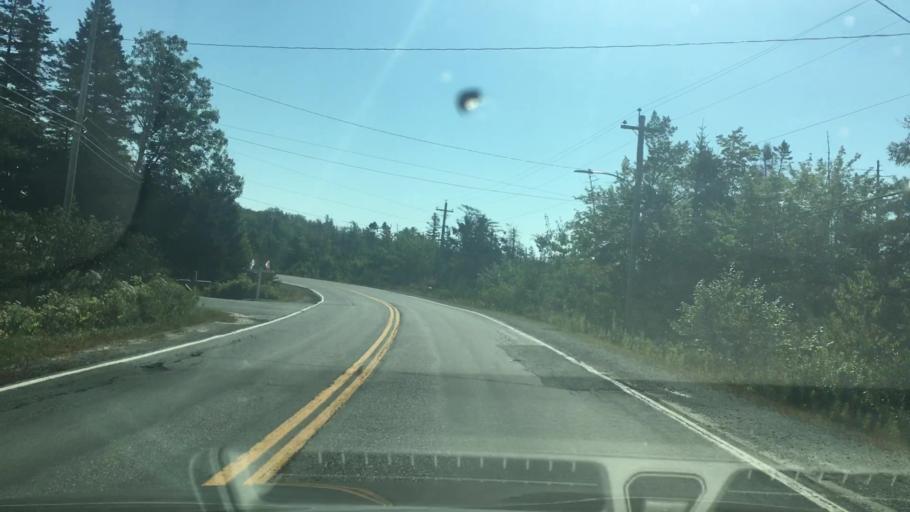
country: CA
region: Nova Scotia
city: Cole Harbour
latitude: 44.7753
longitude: -63.0544
